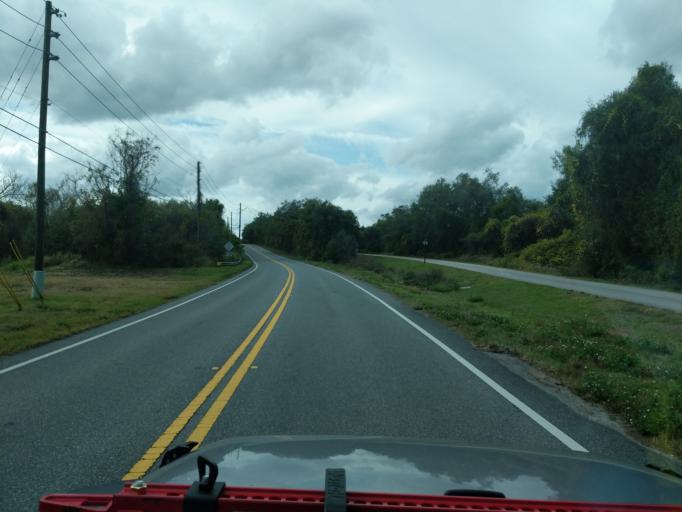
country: US
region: Florida
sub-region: Lake County
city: Clermont
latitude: 28.5686
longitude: -81.8099
